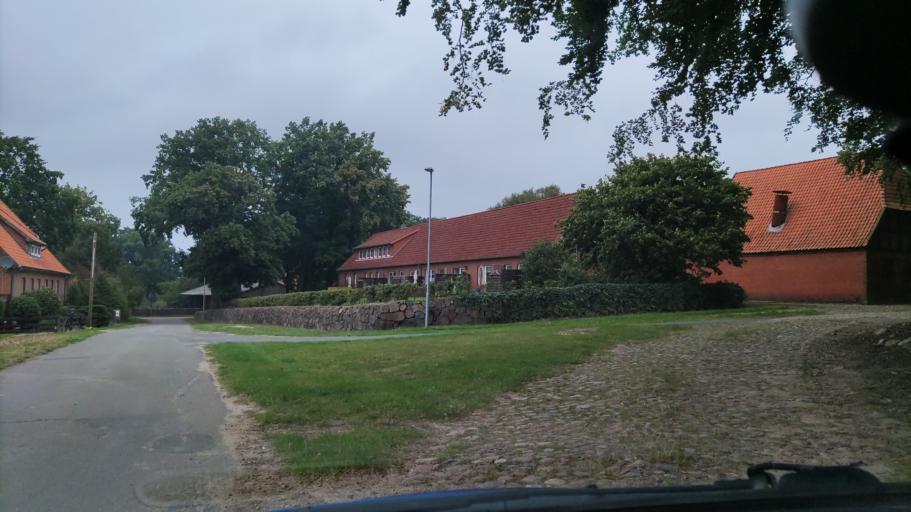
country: DE
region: Lower Saxony
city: Altenmedingen
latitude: 53.1309
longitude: 10.6213
